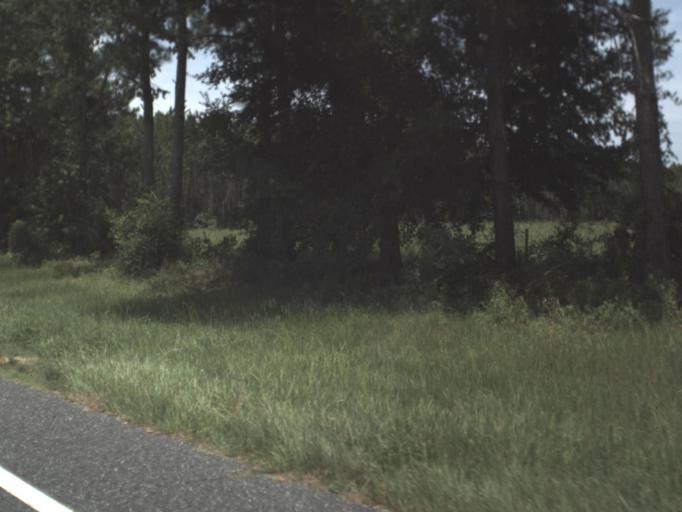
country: US
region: Florida
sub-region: Gilchrist County
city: Trenton
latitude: 29.5697
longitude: -82.8231
